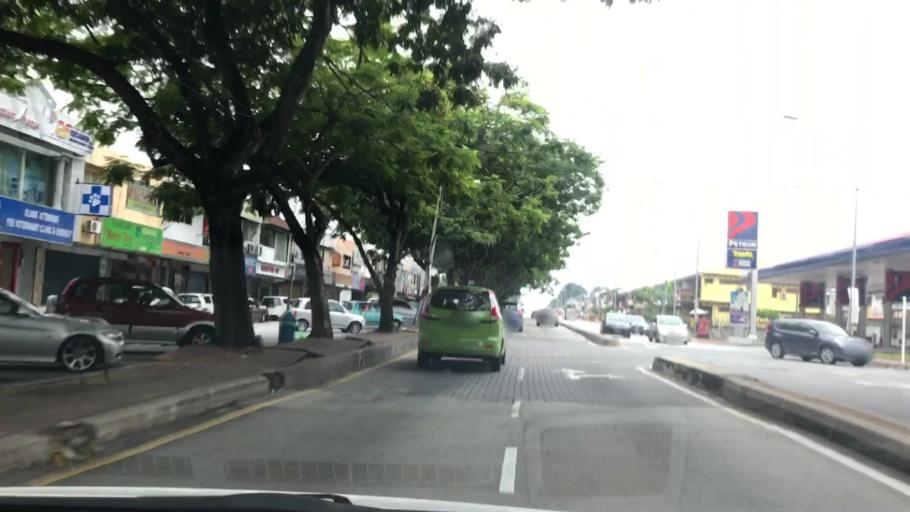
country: MY
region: Selangor
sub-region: Petaling
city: Petaling Jaya
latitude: 3.1145
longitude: 101.6212
